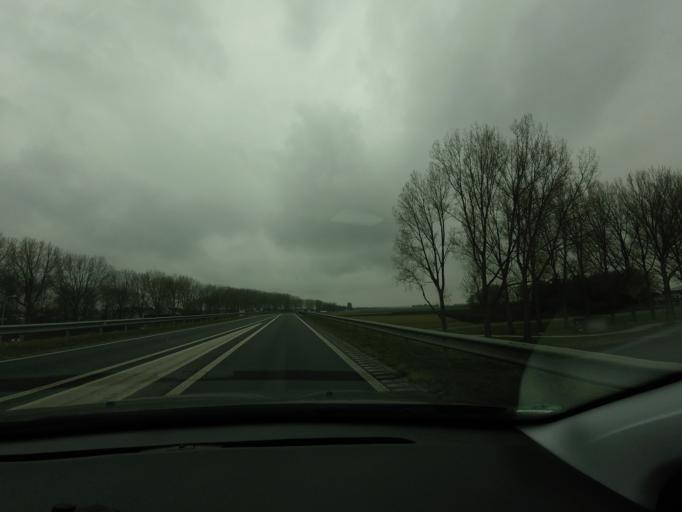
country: NL
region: Flevoland
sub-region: Gemeente Dronten
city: Dronten
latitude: 52.5389
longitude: 5.7391
